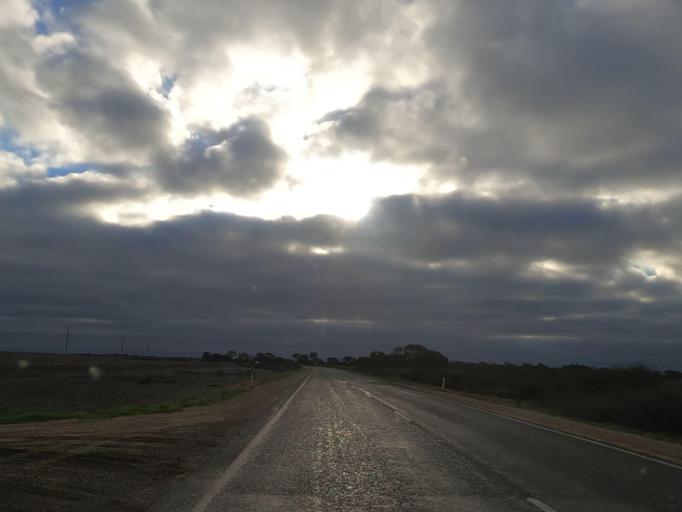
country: AU
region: Victoria
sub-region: Swan Hill
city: Swan Hill
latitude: -35.6528
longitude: 143.8465
